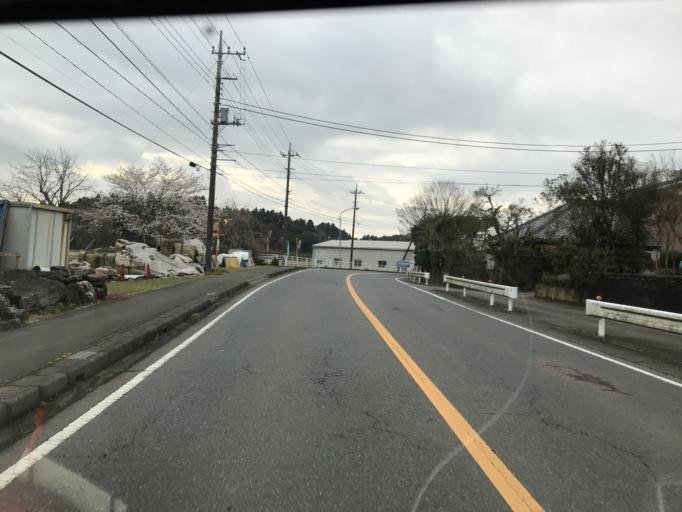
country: JP
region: Chiba
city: Sawara
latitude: 35.8204
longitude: 140.5048
